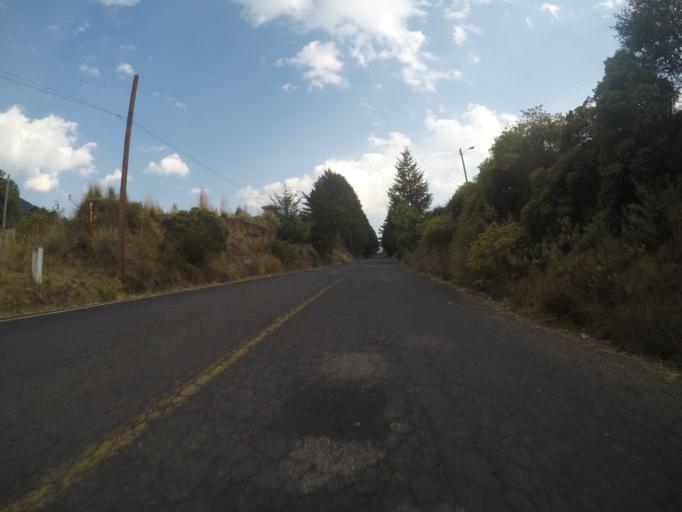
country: MX
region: Mexico
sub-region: Xalatlaco
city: San Juan Tomasquillo Herradura
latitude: 19.1650
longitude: -99.3914
